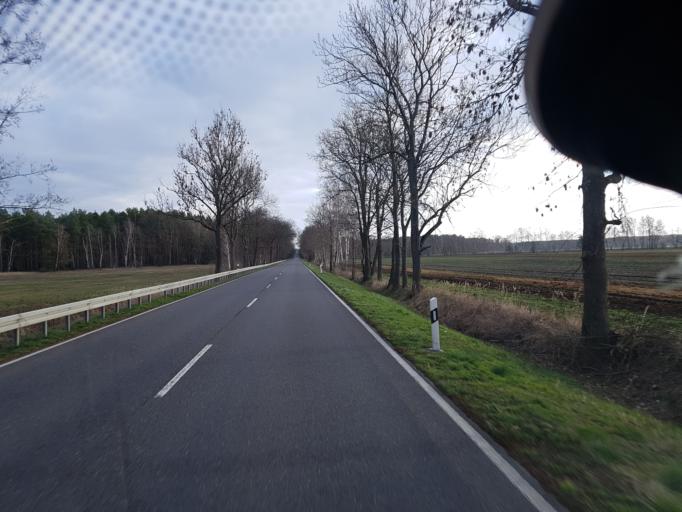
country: DE
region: Brandenburg
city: Luebben
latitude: 51.9732
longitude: 13.9551
